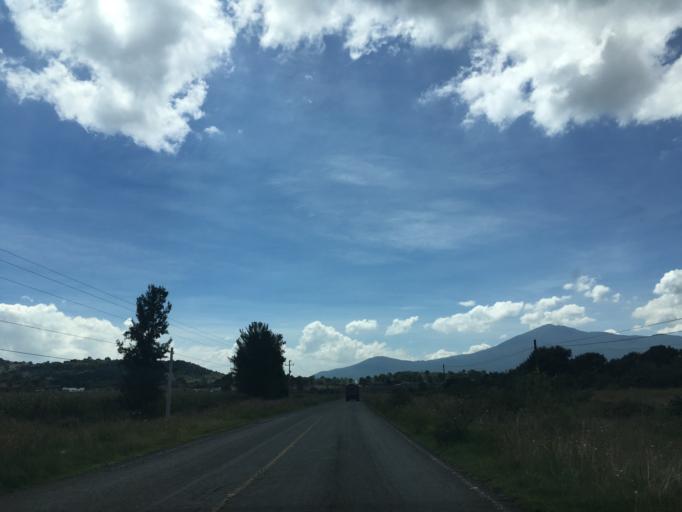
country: MX
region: Michoacan
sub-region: Morelia
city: Cuto de la Esperanza
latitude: 19.7172
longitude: -101.3412
